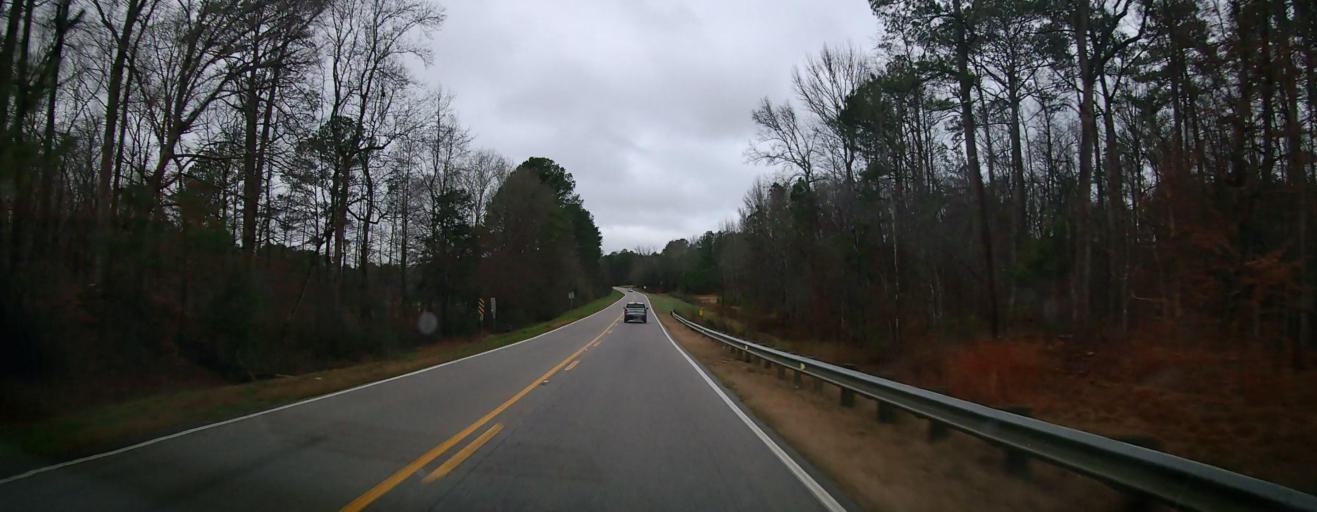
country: US
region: Alabama
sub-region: Bibb County
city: Centreville
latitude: 32.9029
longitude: -87.0017
